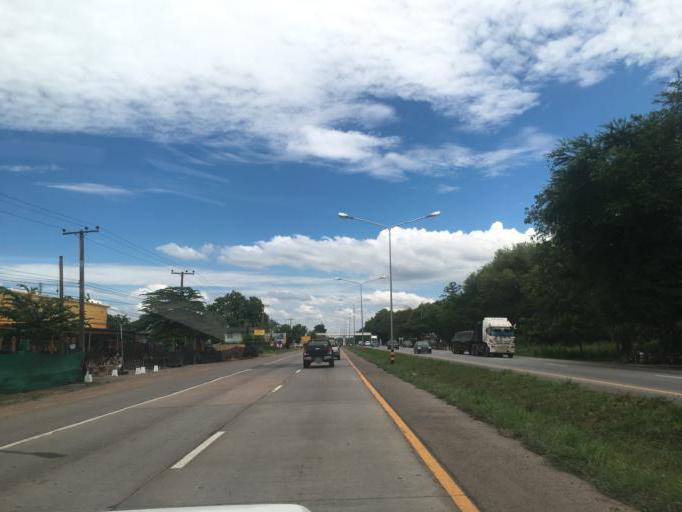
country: TH
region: Khon Kaen
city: Nam Phong
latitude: 16.6342
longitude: 102.7996
